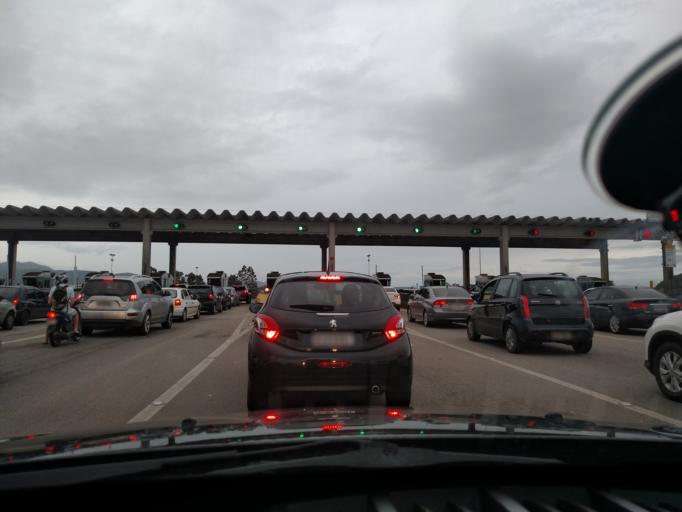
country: BR
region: Santa Catarina
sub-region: Tijucas
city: Tijucas
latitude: -27.1856
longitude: -48.6123
